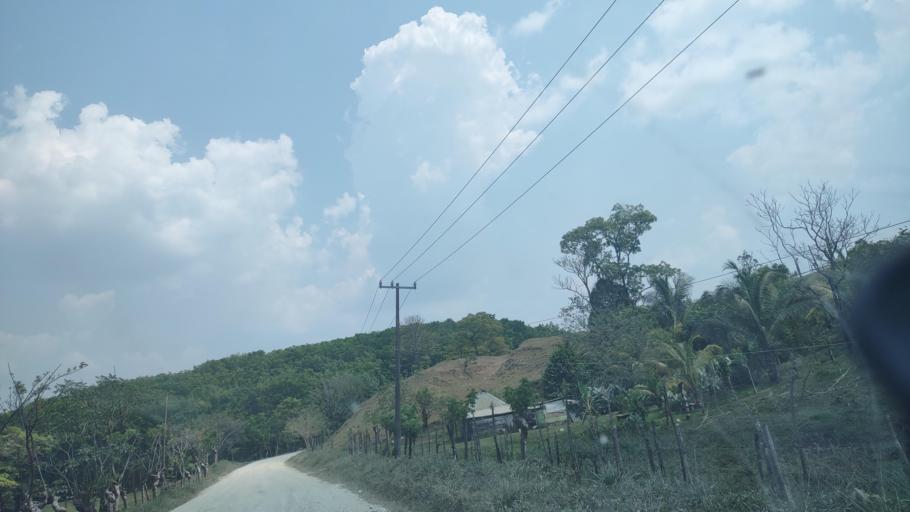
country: MX
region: Tabasco
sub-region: Huimanguillo
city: Francisco Rueda
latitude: 17.6061
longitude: -93.9064
